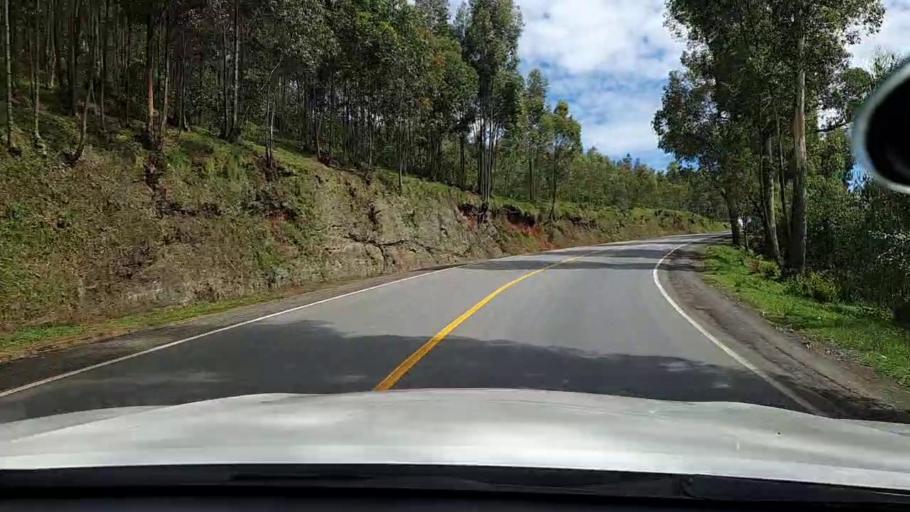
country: RW
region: Kigali
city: Kigali
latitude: -1.8260
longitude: 29.9473
